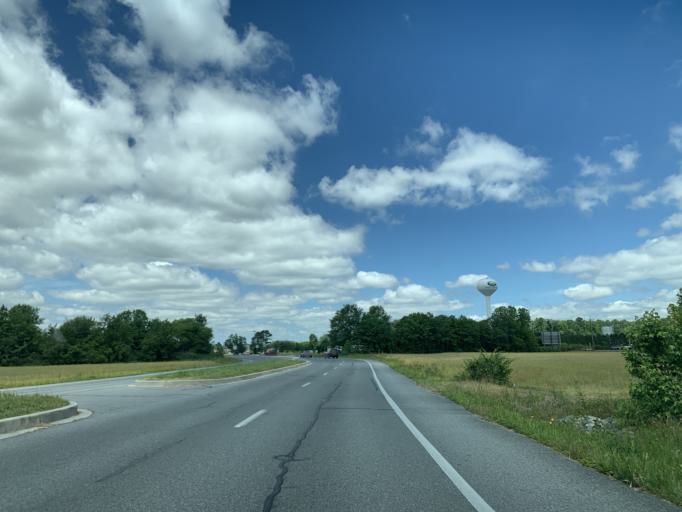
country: US
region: Maryland
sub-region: Worcester County
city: West Ocean City
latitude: 38.3408
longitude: -75.1592
